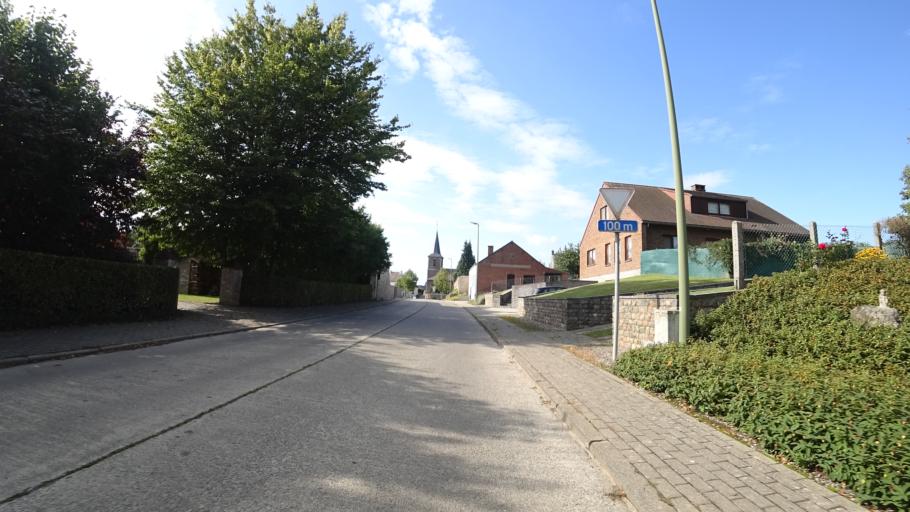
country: BE
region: Wallonia
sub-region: Province du Brabant Wallon
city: Chastre
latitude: 50.5794
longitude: 4.6132
